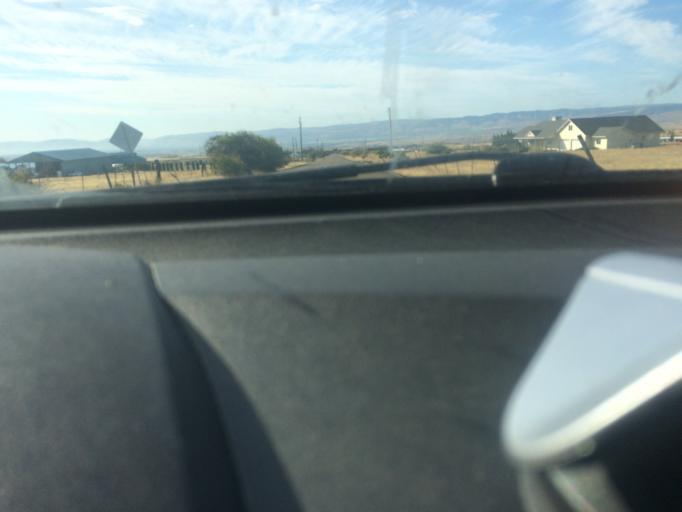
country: US
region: Washington
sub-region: Kittitas County
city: Ellensburg
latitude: 47.1457
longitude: -120.6136
